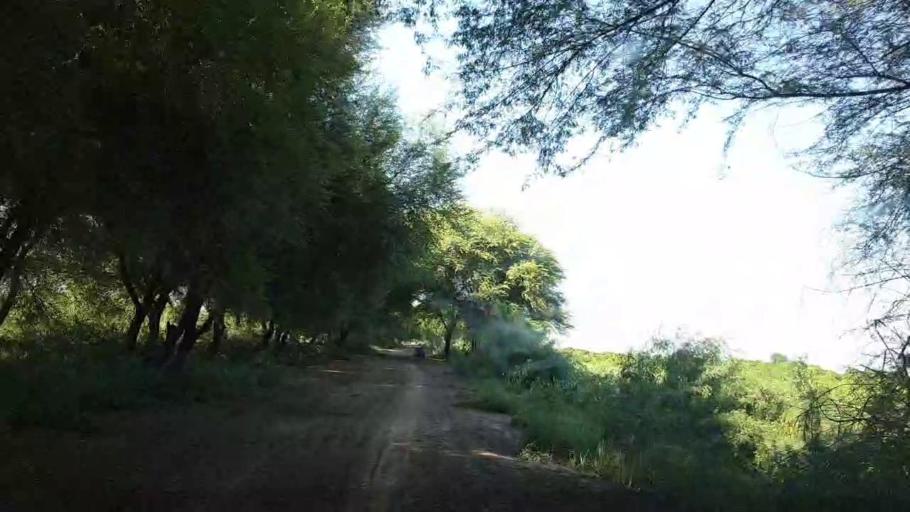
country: PK
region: Sindh
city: Tando Jam
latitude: 25.3577
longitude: 68.5698
